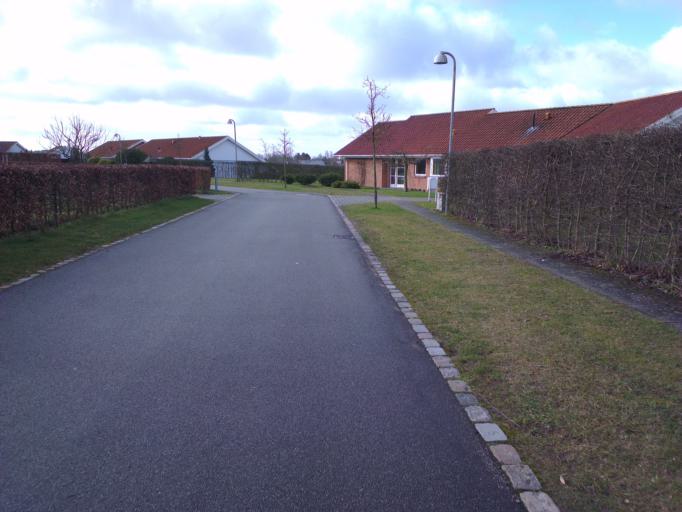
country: DK
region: Capital Region
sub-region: Frederikssund Kommune
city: Frederikssund
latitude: 55.8364
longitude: 12.0838
